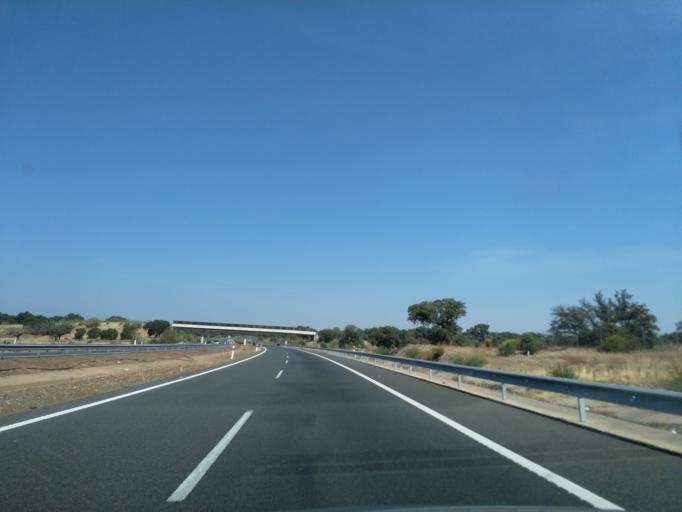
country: ES
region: Extremadura
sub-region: Provincia de Badajoz
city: Mirandilla
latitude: 38.9936
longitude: -6.3294
